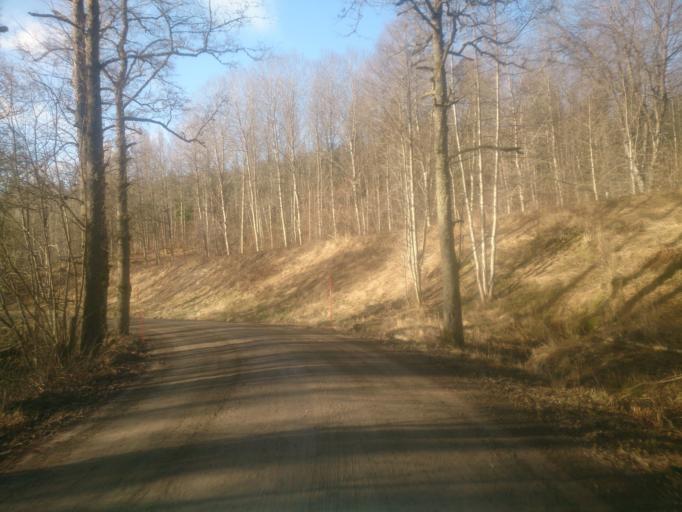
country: SE
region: OEstergoetland
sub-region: Atvidabergs Kommun
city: Atvidaberg
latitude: 58.1829
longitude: 16.1118
